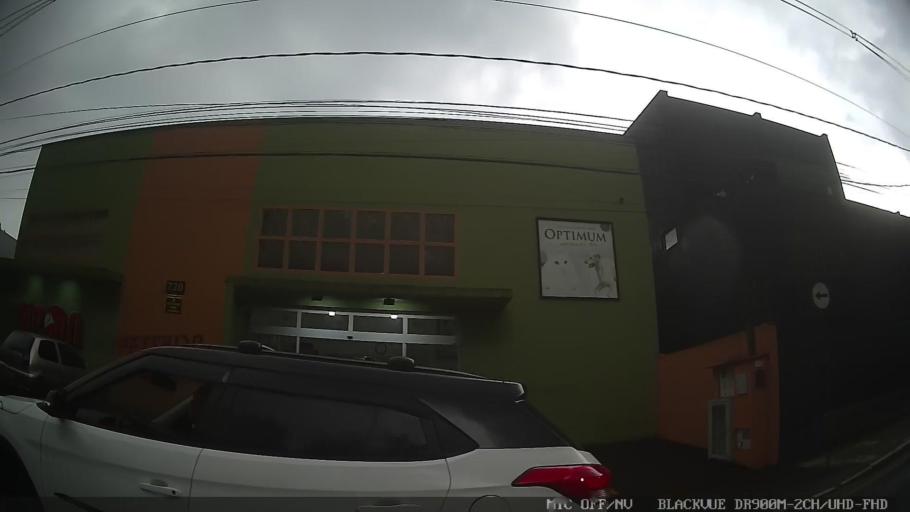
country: BR
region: Sao Paulo
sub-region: Ribeirao Pires
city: Ribeirao Pires
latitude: -23.7189
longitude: -46.4076
